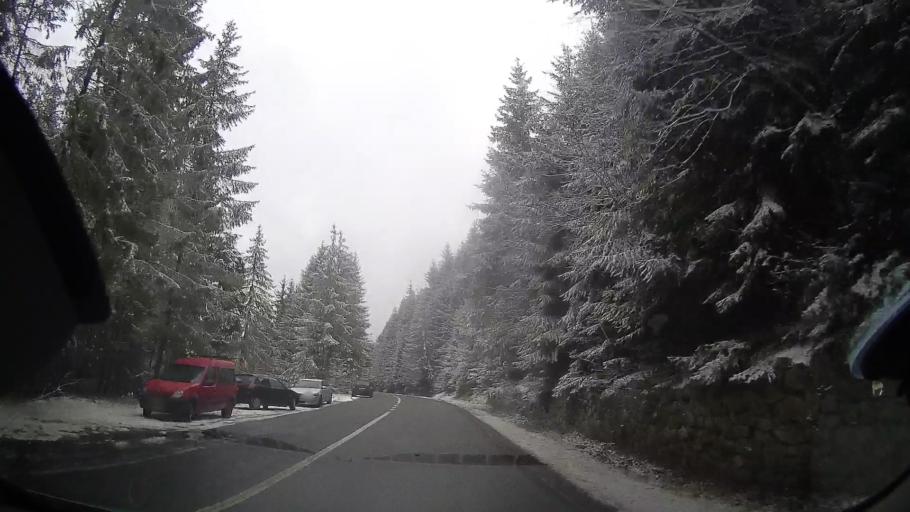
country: RO
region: Cluj
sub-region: Comuna Belis
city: Belis
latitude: 46.6710
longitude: 23.0511
